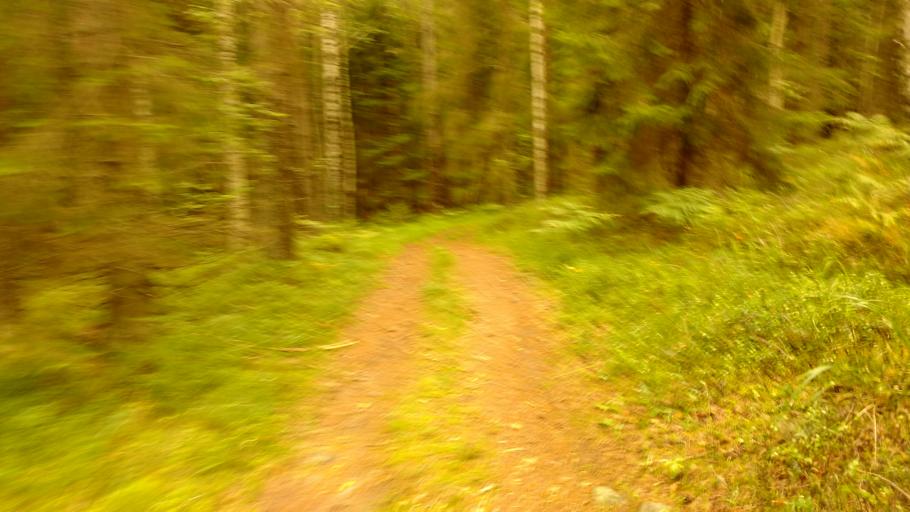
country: FI
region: Varsinais-Suomi
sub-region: Salo
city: Pertteli
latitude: 60.4016
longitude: 23.2202
